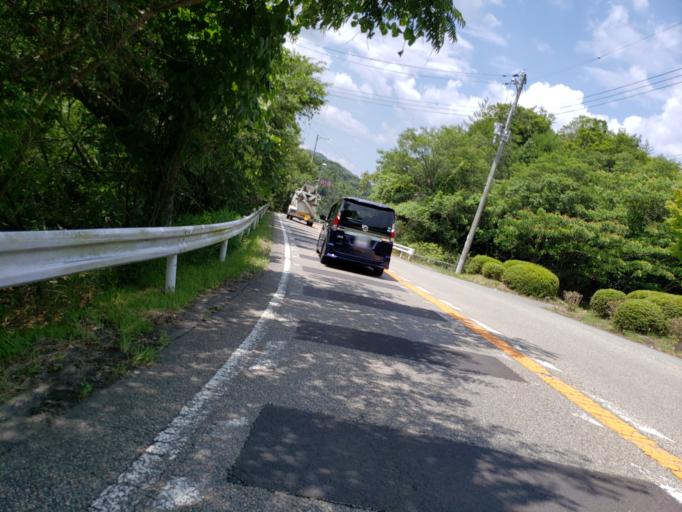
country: JP
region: Hyogo
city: Aioi
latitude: 34.7936
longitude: 134.4485
